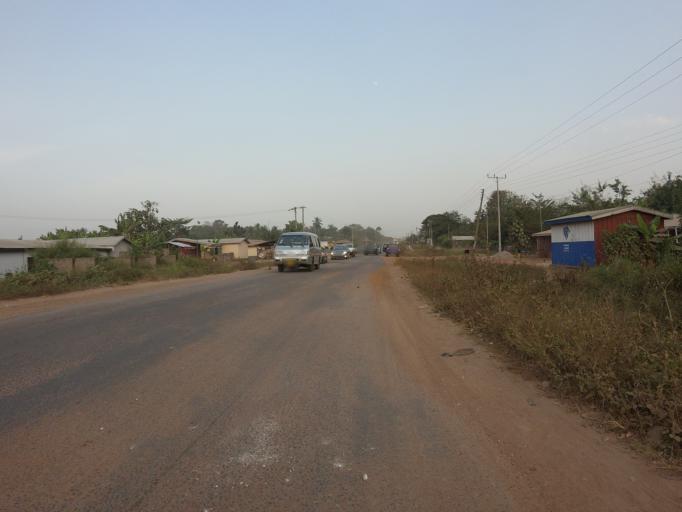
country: GH
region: Volta
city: Ho
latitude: 6.5749
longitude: 0.4151
